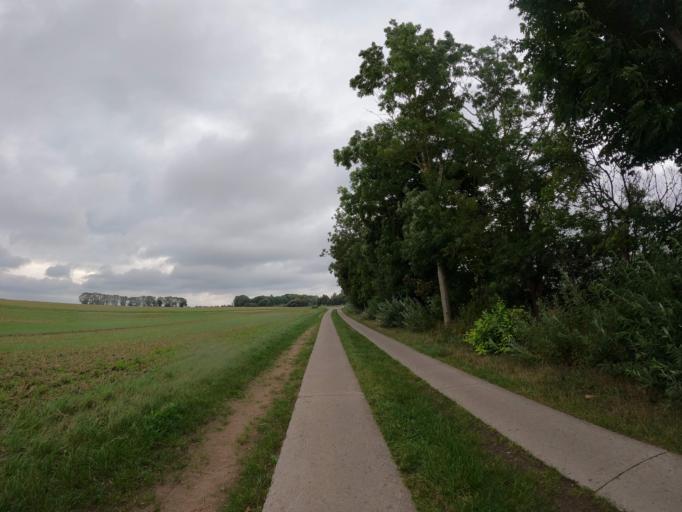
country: DE
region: Mecklenburg-Vorpommern
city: Garz
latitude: 54.2944
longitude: 13.3289
